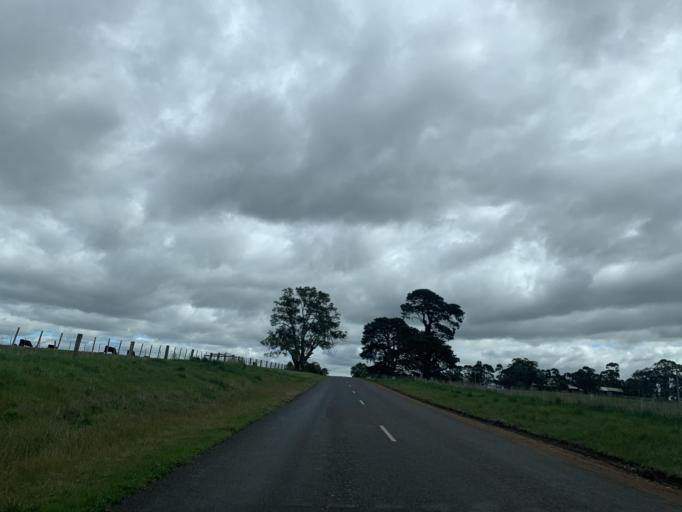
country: AU
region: Victoria
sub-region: Whittlesea
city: Whittlesea
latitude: -37.1859
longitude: 145.0298
